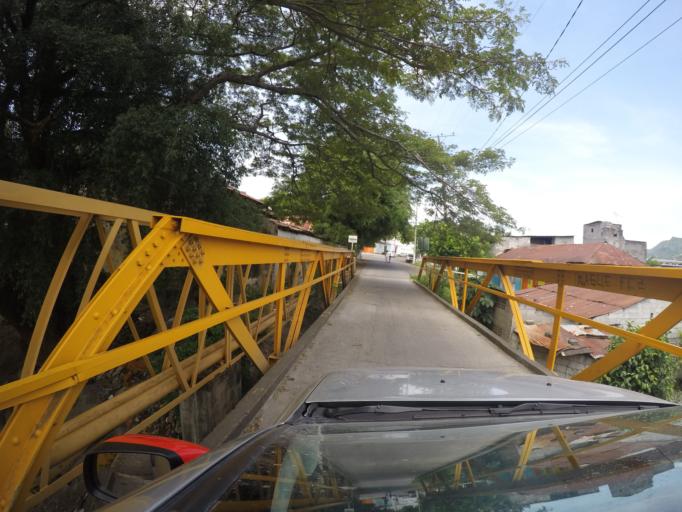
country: CO
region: Tolima
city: Honda
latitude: 5.2051
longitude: -74.7357
